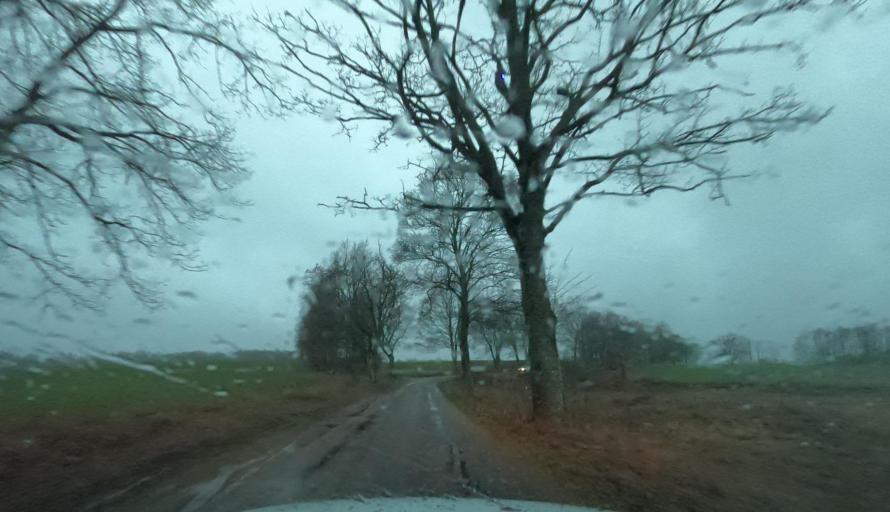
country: PL
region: West Pomeranian Voivodeship
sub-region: Powiat szczecinecki
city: Borne Sulinowo
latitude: 53.6968
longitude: 16.5040
